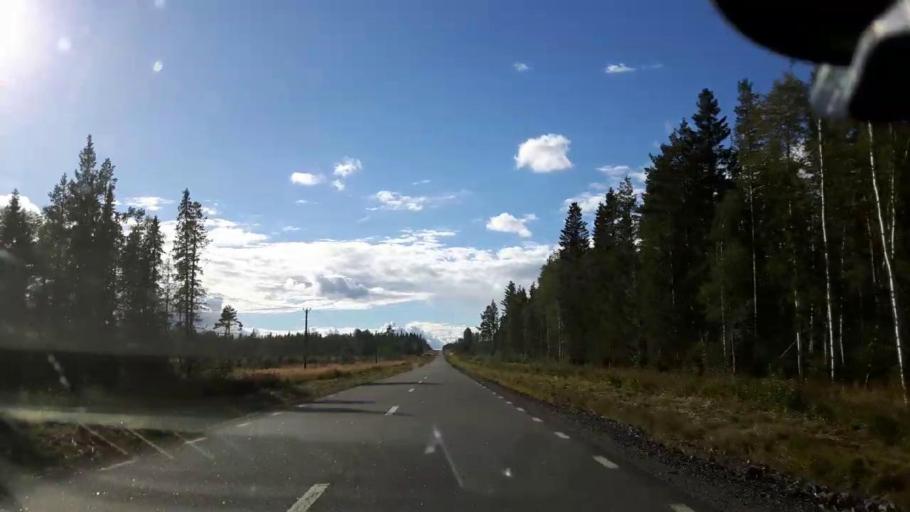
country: SE
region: Jaemtland
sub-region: Stroemsunds Kommun
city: Stroemsund
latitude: 63.5410
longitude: 15.9631
